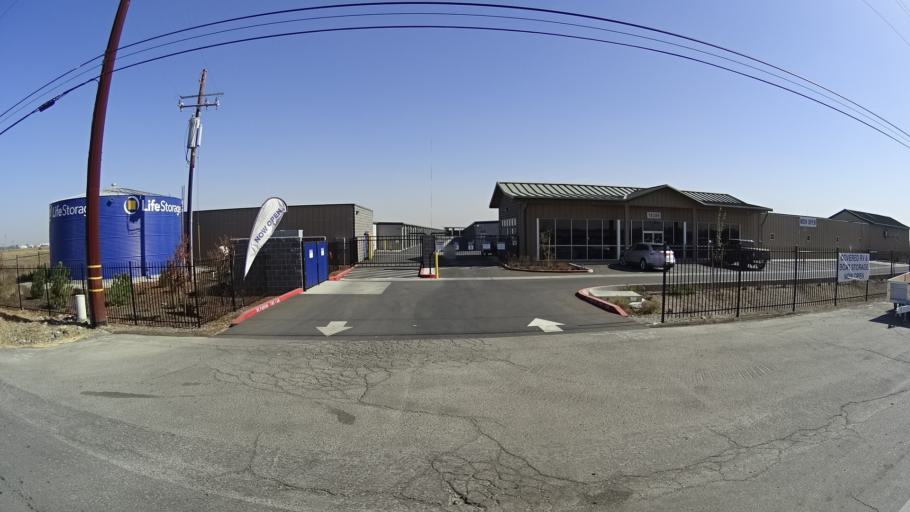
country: US
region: California
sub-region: Yolo County
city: Woodland
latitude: 38.6572
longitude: -121.7287
